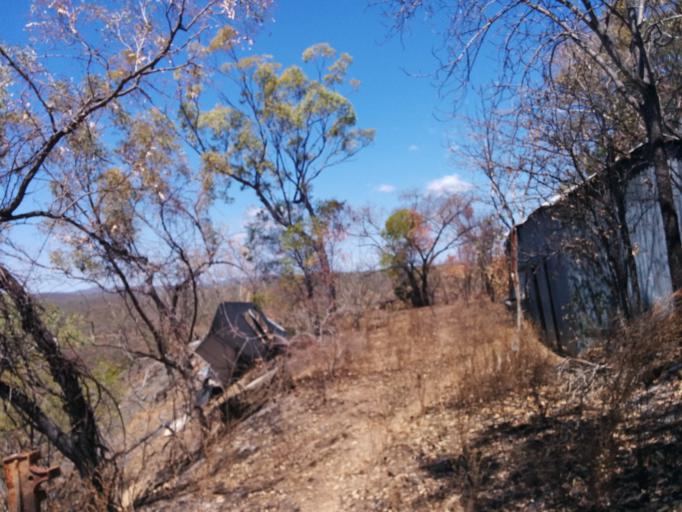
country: AU
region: Queensland
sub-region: Tablelands
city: Mareeba
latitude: -16.9215
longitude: 145.0302
